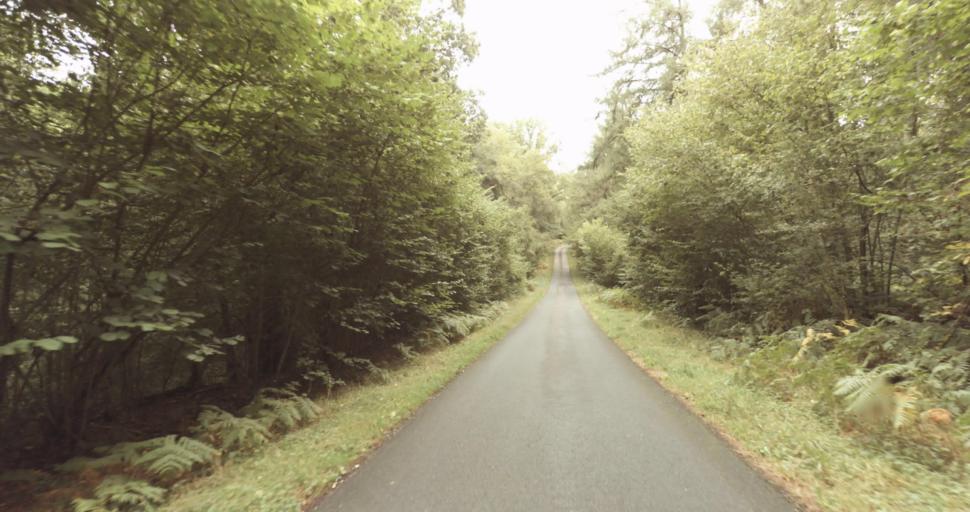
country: FR
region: Lower Normandy
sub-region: Departement de l'Orne
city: Gace
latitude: 48.8457
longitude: 0.3287
